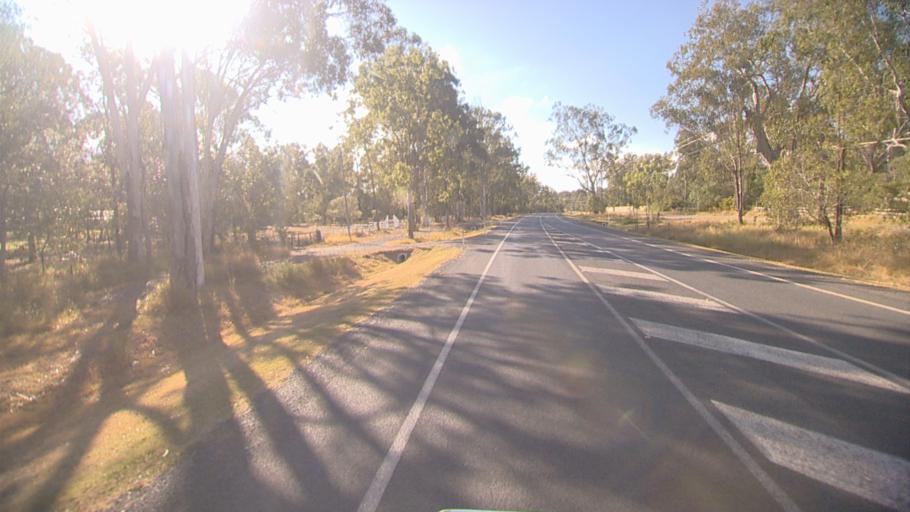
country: AU
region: Queensland
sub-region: Logan
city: North Maclean
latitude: -27.7830
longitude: 152.9805
